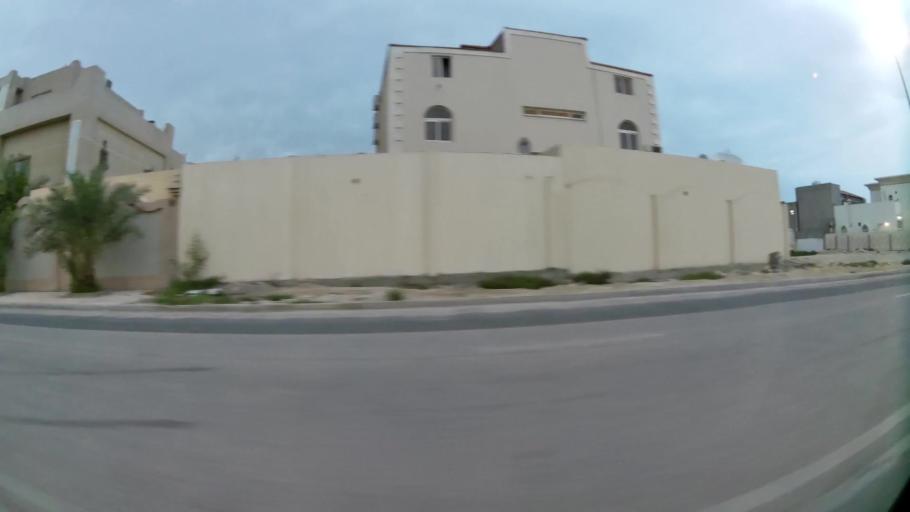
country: QA
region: Baladiyat ad Dawhah
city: Doha
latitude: 25.3463
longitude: 51.5096
